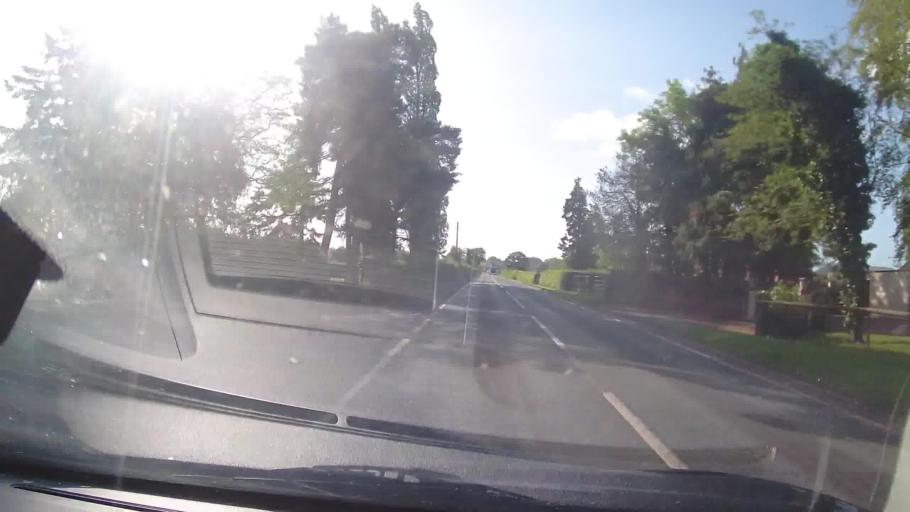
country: GB
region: England
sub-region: Shropshire
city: Wem
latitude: 52.8480
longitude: -2.7224
